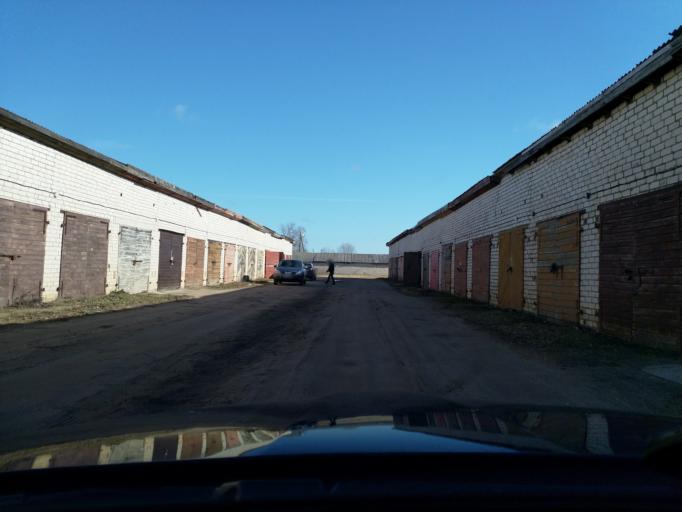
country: LV
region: Kuldigas Rajons
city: Kuldiga
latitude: 56.9753
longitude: 21.9477
